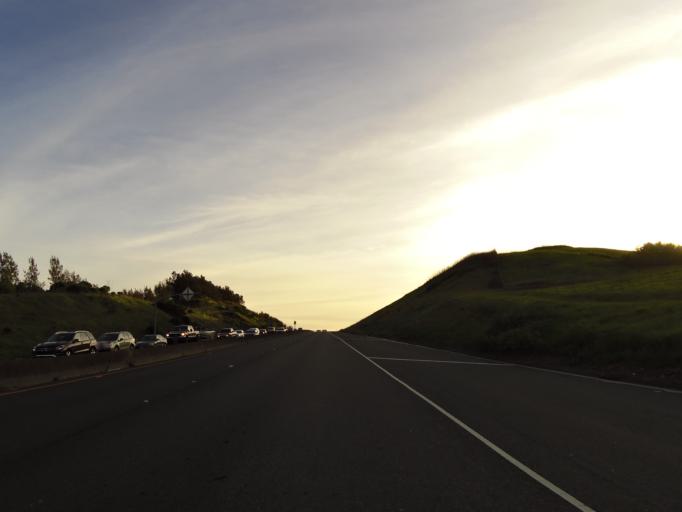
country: US
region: California
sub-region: Marin County
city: Black Point-Green Point
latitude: 38.1493
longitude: -122.4521
